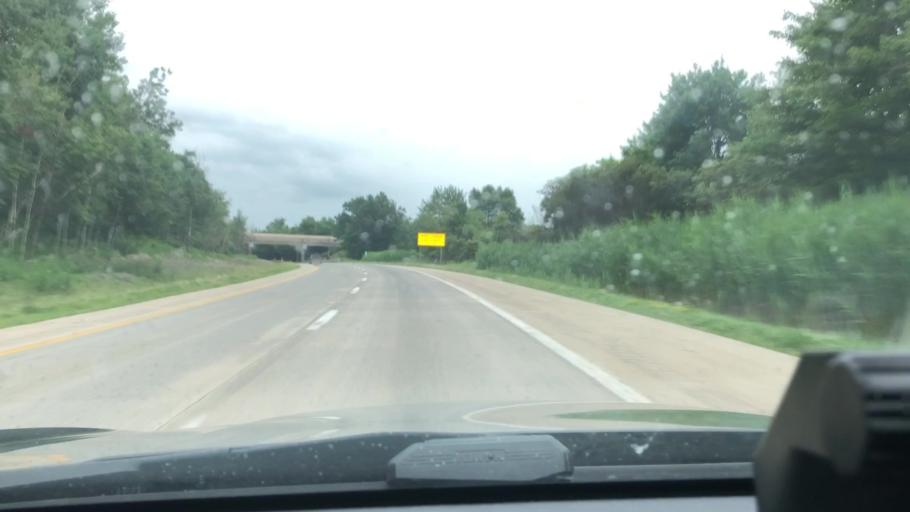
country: US
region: Pennsylvania
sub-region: Monroe County
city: Emerald Lakes
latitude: 41.0725
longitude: -75.3967
